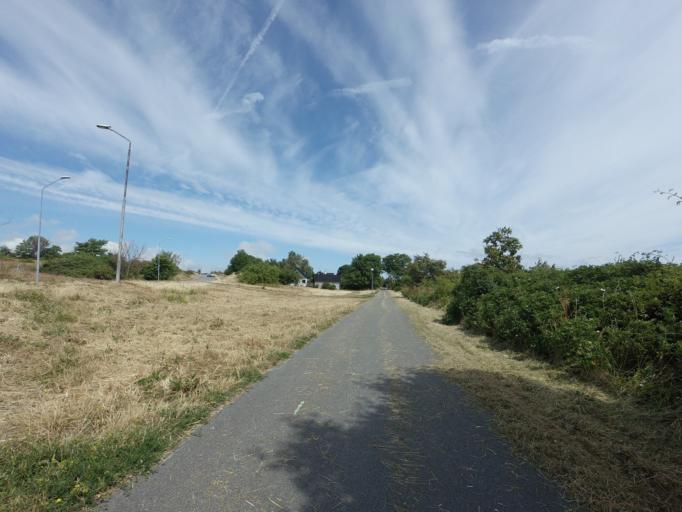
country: SE
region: Skane
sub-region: Simrishamns Kommun
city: Simrishamn
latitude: 55.5401
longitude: 14.3560
